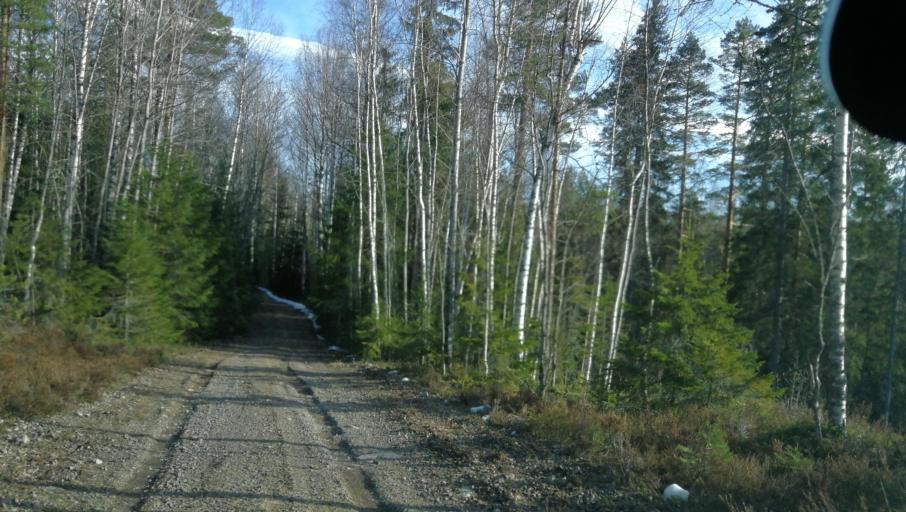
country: SE
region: Dalarna
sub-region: Vansbro Kommun
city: Vansbro
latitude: 60.7957
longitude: 14.2330
